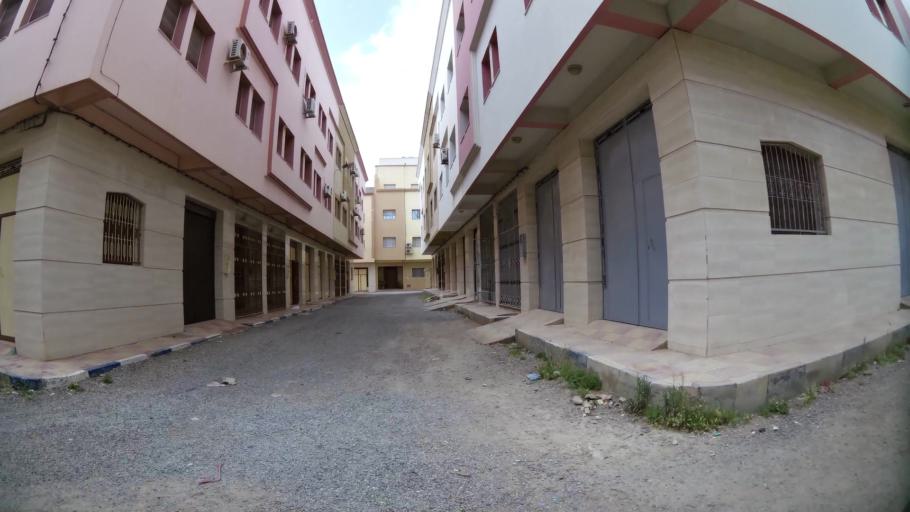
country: MA
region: Oriental
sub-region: Nador
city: Nador
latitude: 35.1654
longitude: -2.9205
